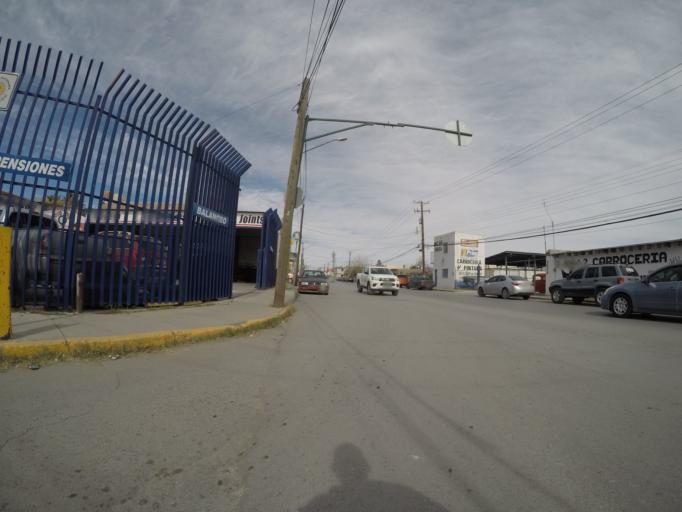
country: MX
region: Chihuahua
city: Ciudad Juarez
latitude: 31.7117
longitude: -106.4343
